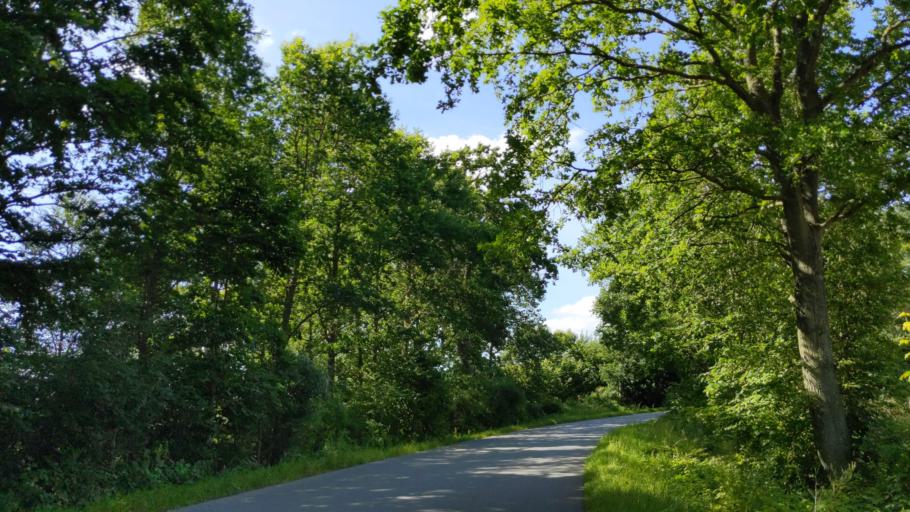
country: DE
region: Schleswig-Holstein
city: Neustadt in Holstein
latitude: 54.1354
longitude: 10.7716
